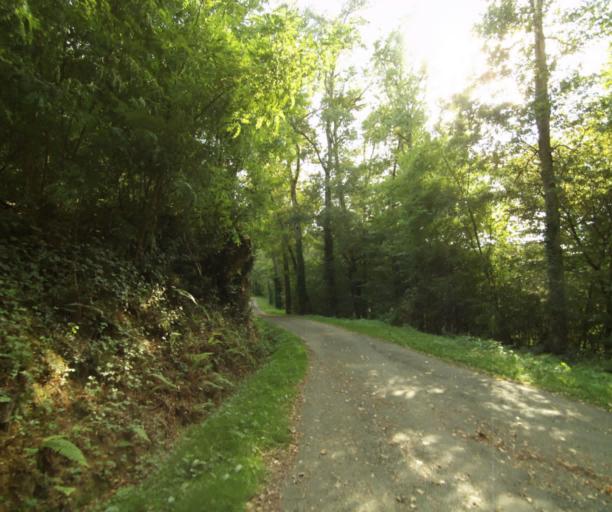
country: FR
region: Midi-Pyrenees
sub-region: Departement du Gers
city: Cazaubon
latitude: 43.9056
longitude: -0.1107
